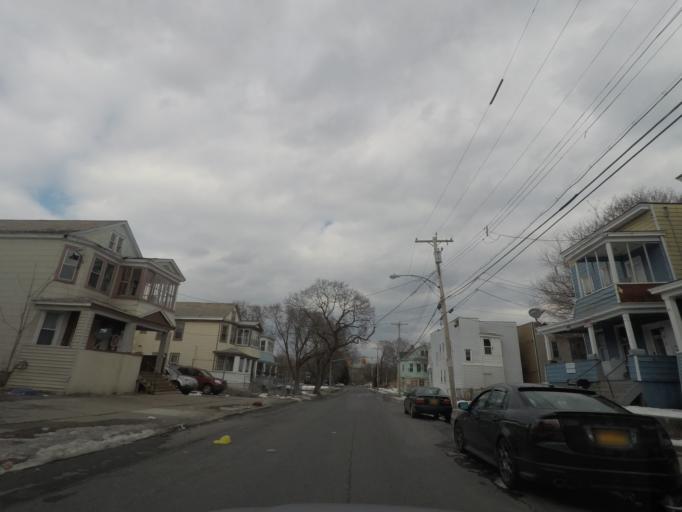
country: US
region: New York
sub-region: Albany County
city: Albany
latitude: 42.6669
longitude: -73.7674
